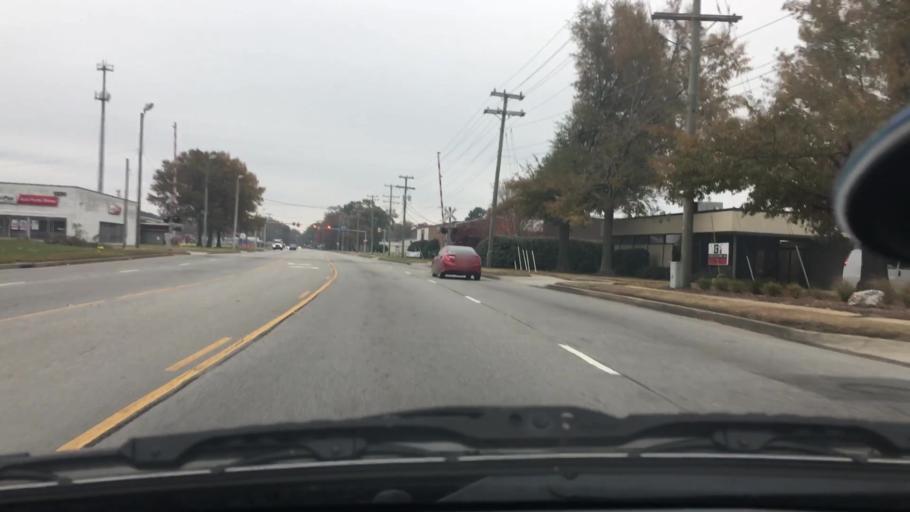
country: US
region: Virginia
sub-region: City of Norfolk
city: Norfolk
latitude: 36.8605
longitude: -76.2433
